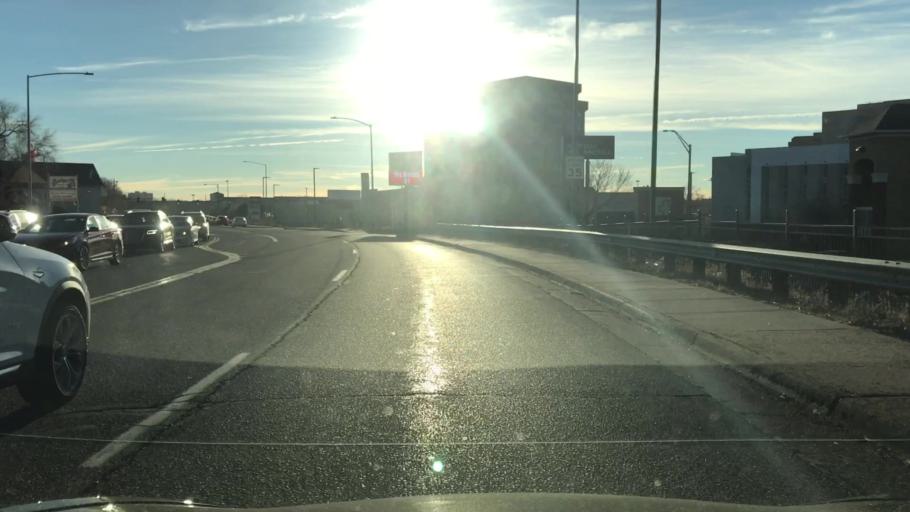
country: US
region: Colorado
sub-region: Arapahoe County
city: Glendale
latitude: 39.7106
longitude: -104.9358
